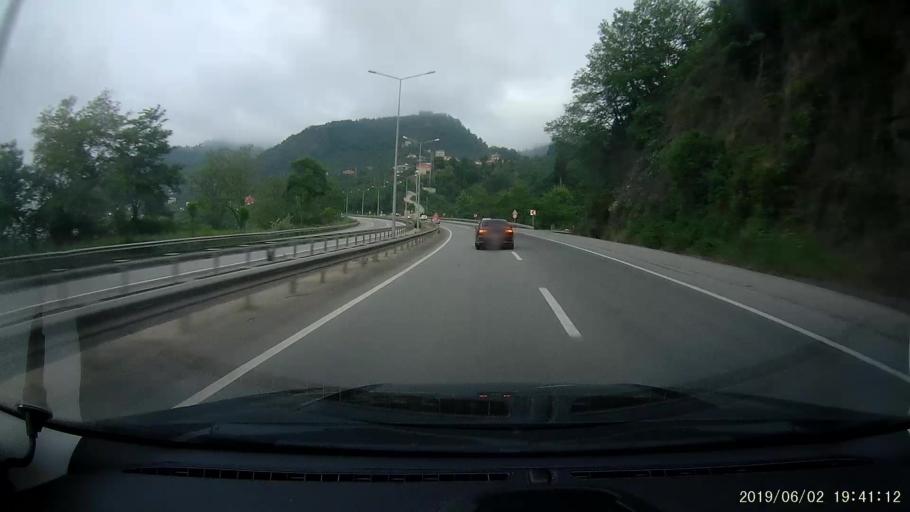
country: TR
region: Giresun
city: Kesap
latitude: 40.9155
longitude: 38.4754
